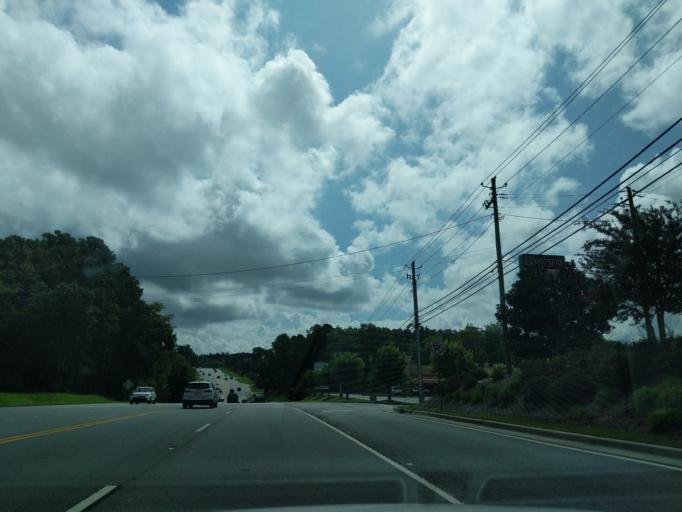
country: US
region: Georgia
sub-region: Columbia County
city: Evans
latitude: 33.5473
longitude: -82.1486
